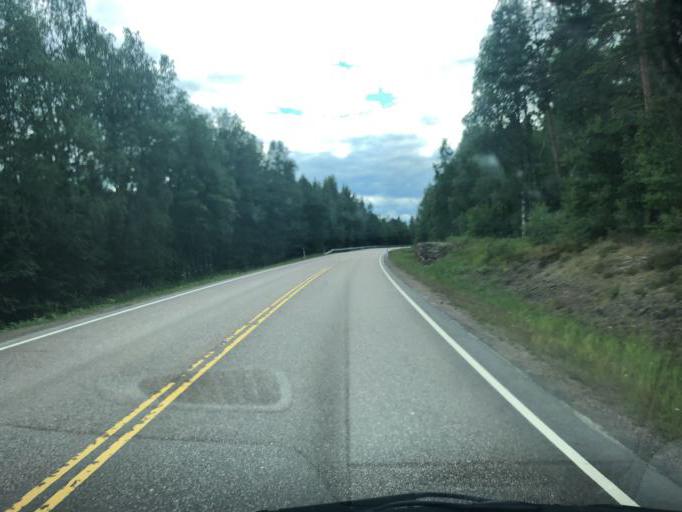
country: FI
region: Southern Savonia
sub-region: Mikkeli
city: Maentyharju
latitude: 61.1441
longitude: 27.1219
